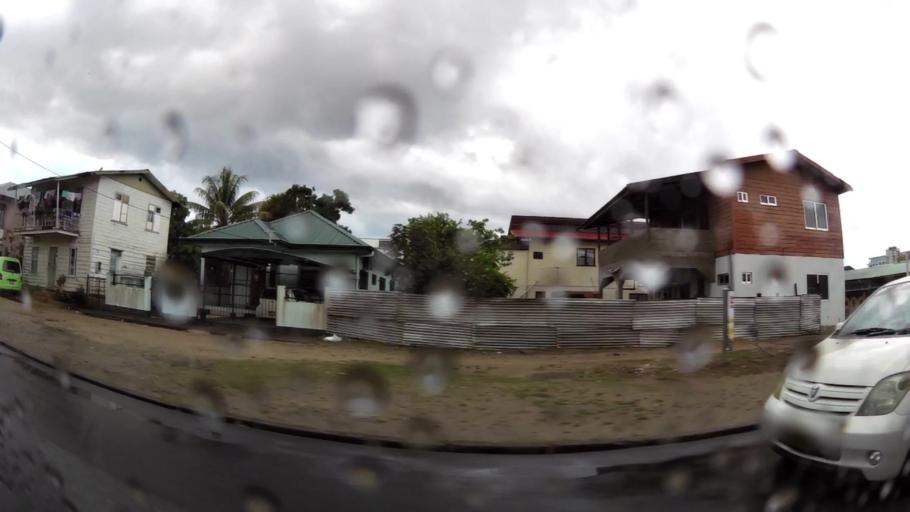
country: SR
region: Paramaribo
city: Paramaribo
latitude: 5.8310
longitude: -55.1675
